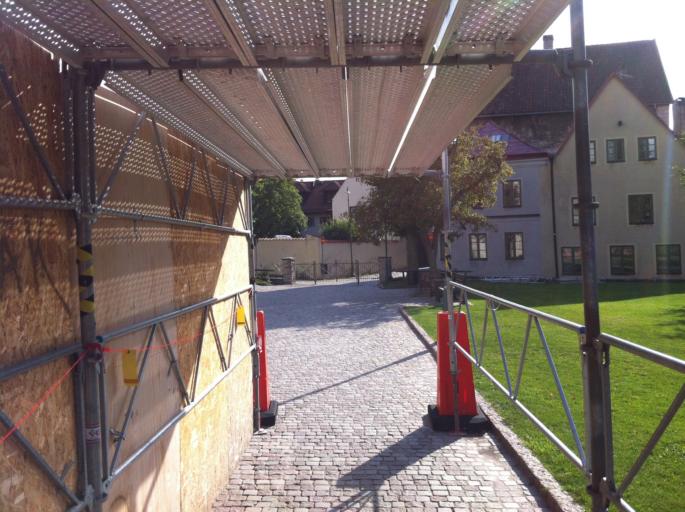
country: SE
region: Gotland
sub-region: Gotland
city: Visby
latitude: 57.6418
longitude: 18.2976
